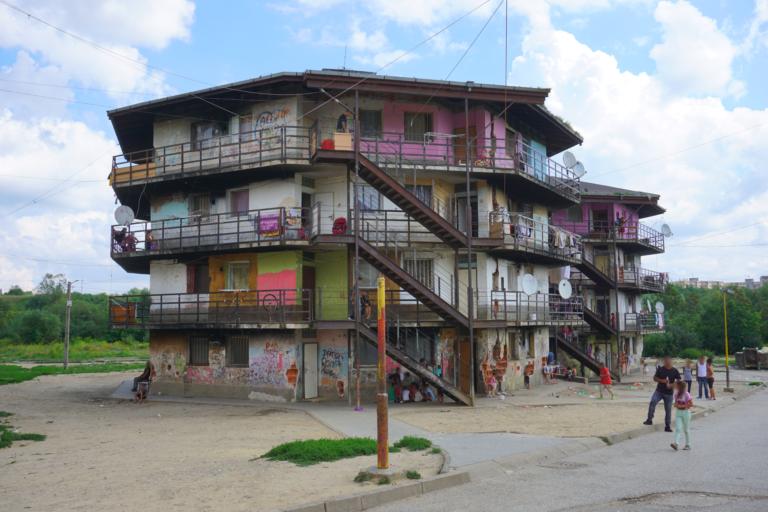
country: SK
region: Kosicky
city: Kosice
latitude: 48.6965
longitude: 21.2240
